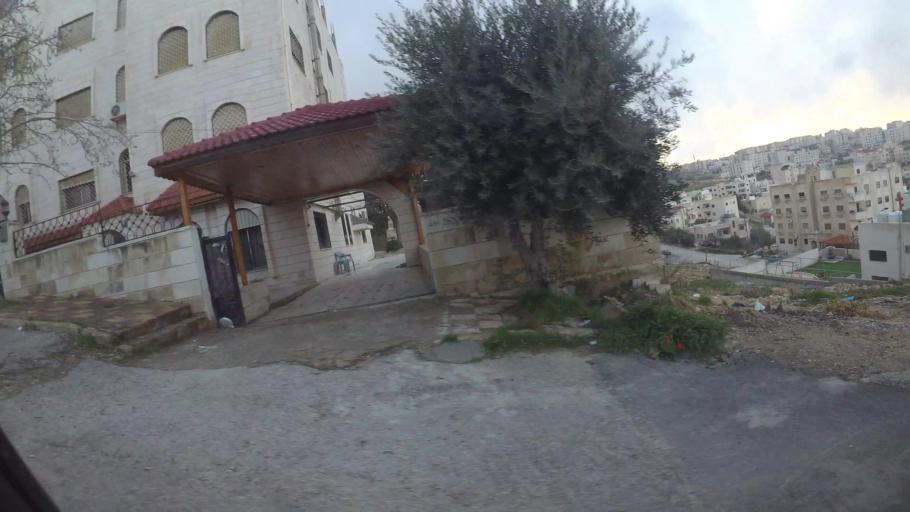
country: JO
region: Amman
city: Al Jubayhah
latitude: 32.0499
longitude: 35.8934
